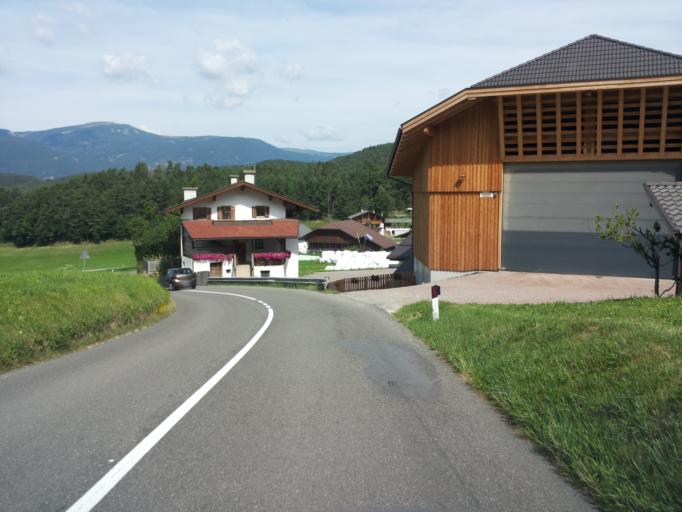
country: IT
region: Trentino-Alto Adige
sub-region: Bolzano
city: Castelrotto
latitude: 46.5718
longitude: 11.5797
